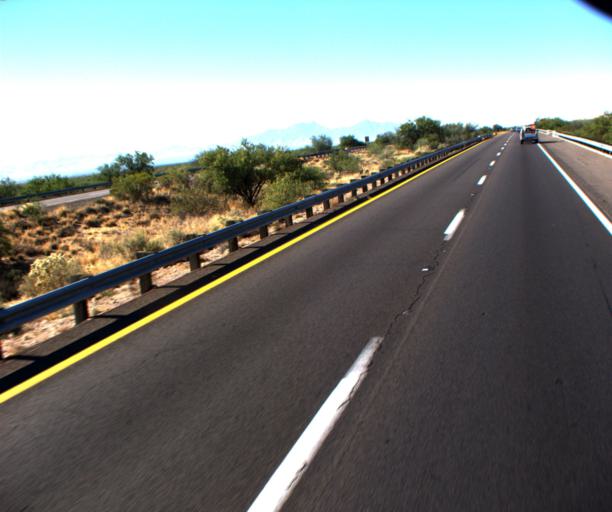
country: US
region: Arizona
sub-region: Pima County
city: Summit
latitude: 32.0528
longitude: -110.9930
